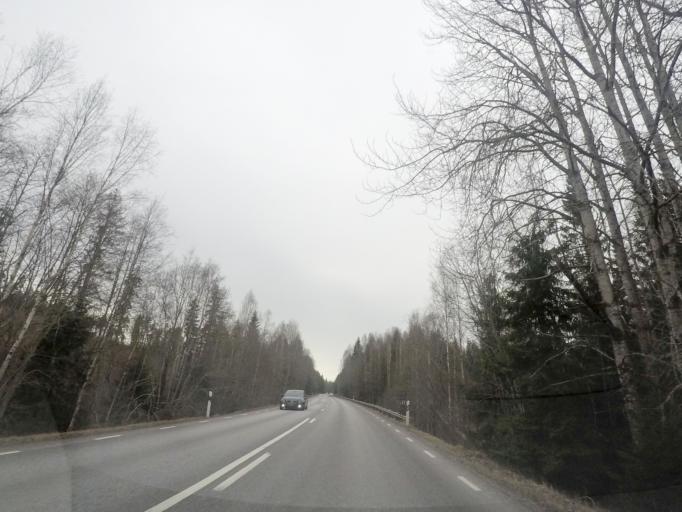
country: SE
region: Vaestmanland
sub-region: Skinnskattebergs Kommun
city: Skinnskatteberg
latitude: 59.8455
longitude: 15.6763
